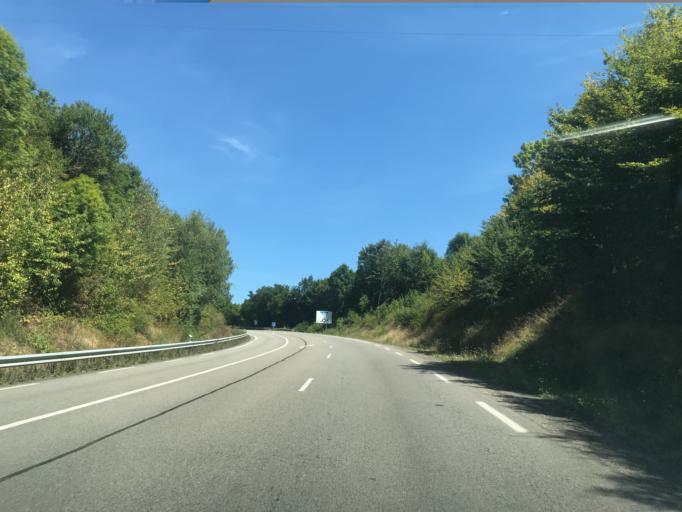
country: FR
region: Limousin
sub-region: Departement de la Correze
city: Tulle
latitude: 45.2806
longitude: 1.7956
